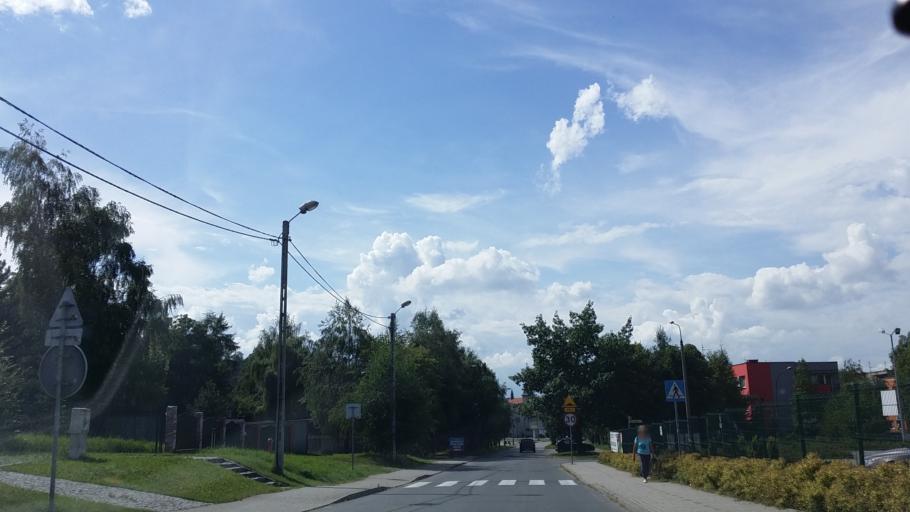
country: PL
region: Lesser Poland Voivodeship
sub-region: Powiat myslenicki
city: Dobczyce
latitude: 49.8793
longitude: 20.0975
